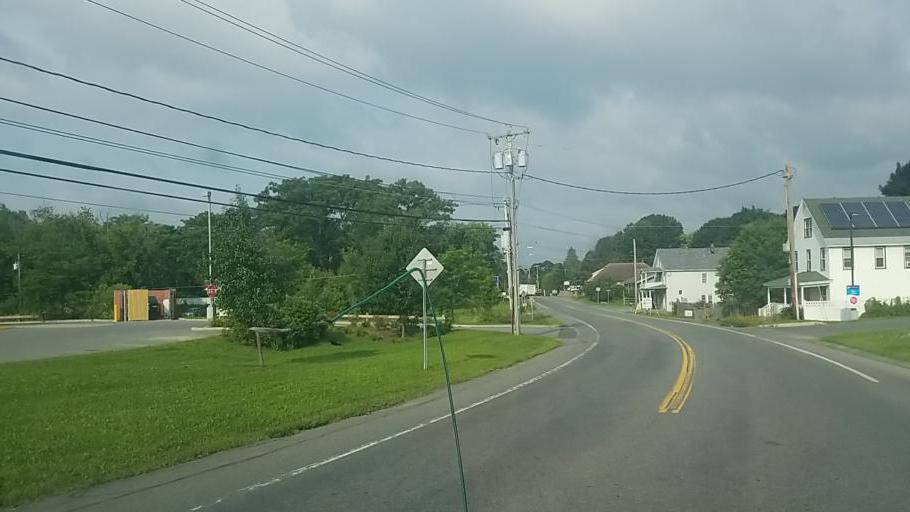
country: US
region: New York
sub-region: Fulton County
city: Gloversville
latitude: 43.0515
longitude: -74.3231
